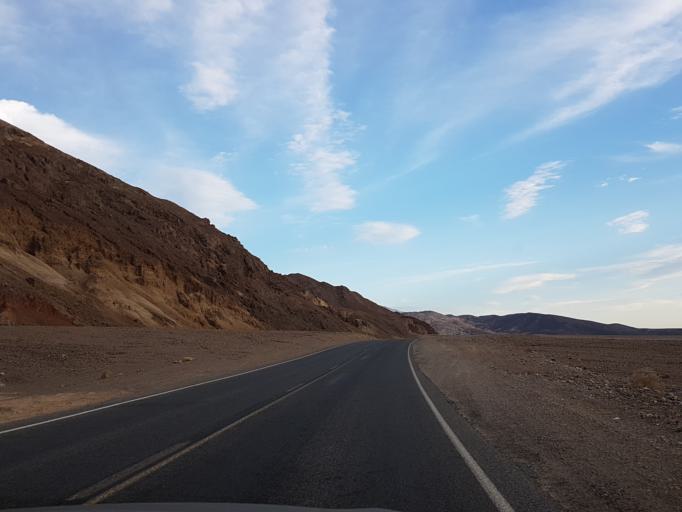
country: US
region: Nevada
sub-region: Nye County
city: Beatty
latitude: 36.4274
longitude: -116.8498
